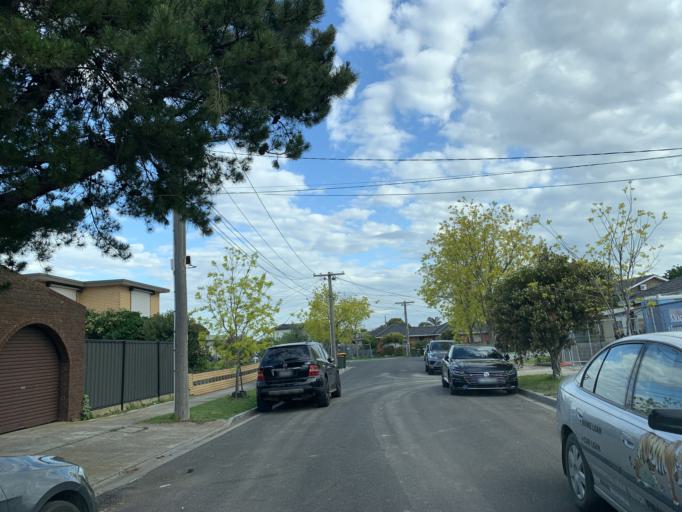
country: AU
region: Victoria
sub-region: Moonee Valley
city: Essendon West
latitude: -37.7596
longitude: 144.8597
